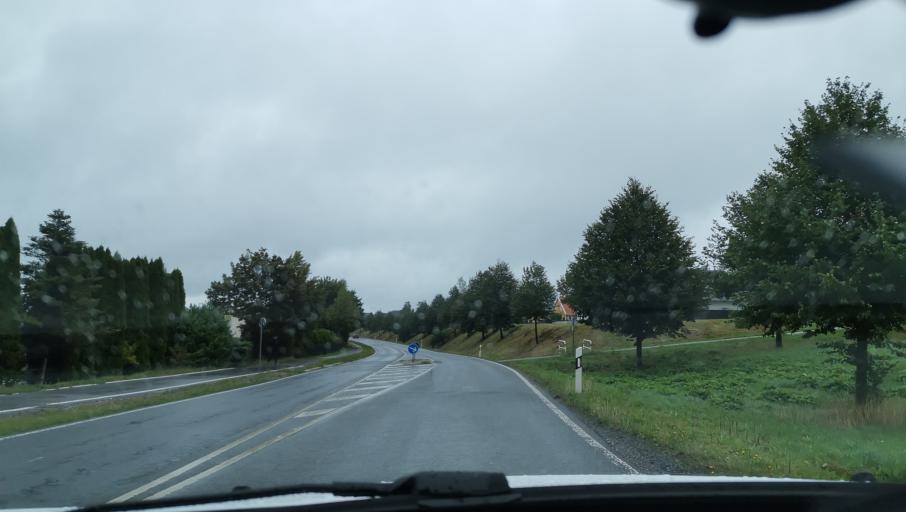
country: DE
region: North Rhine-Westphalia
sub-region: Regierungsbezirk Arnsberg
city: Breckerfeld
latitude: 51.2497
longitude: 7.4666
